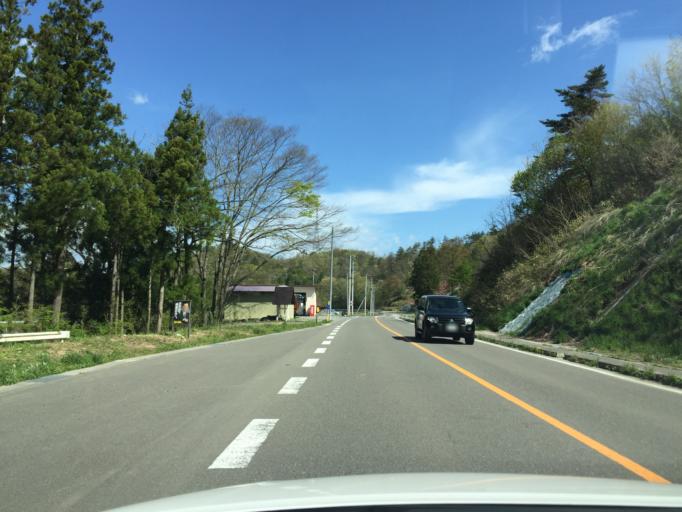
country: JP
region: Fukushima
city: Funehikimachi-funehiki
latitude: 37.5404
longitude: 140.5359
